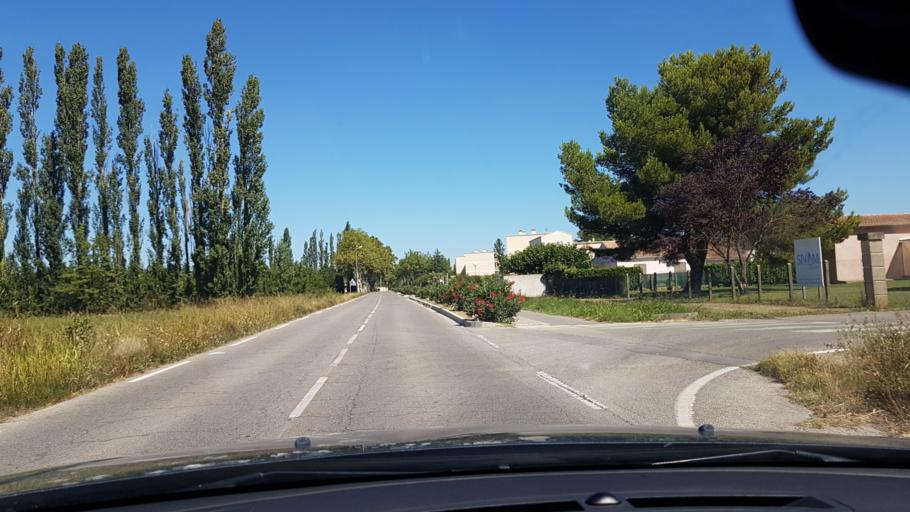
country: FR
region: Provence-Alpes-Cote d'Azur
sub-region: Departement des Bouches-du-Rhone
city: Saint-Andiol
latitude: 43.8235
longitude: 4.9467
